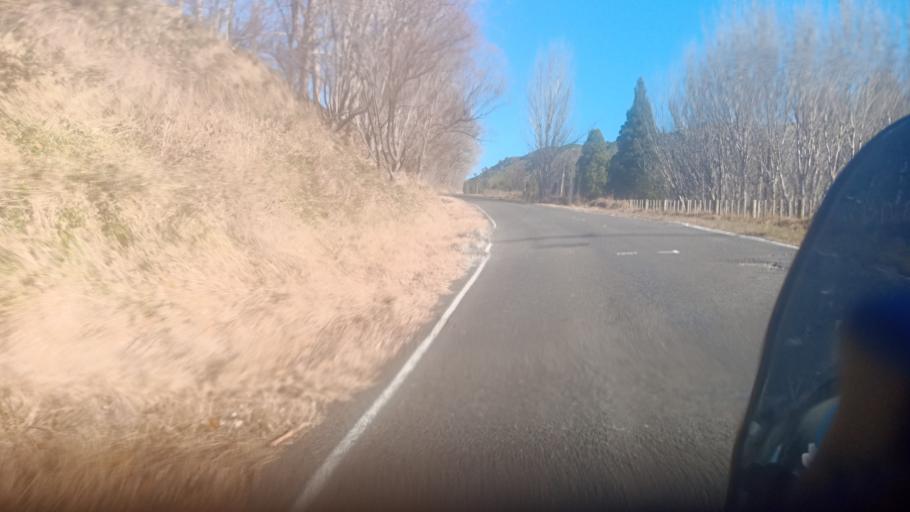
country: NZ
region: Gisborne
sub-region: Gisborne District
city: Gisborne
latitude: -38.5631
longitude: 177.6134
